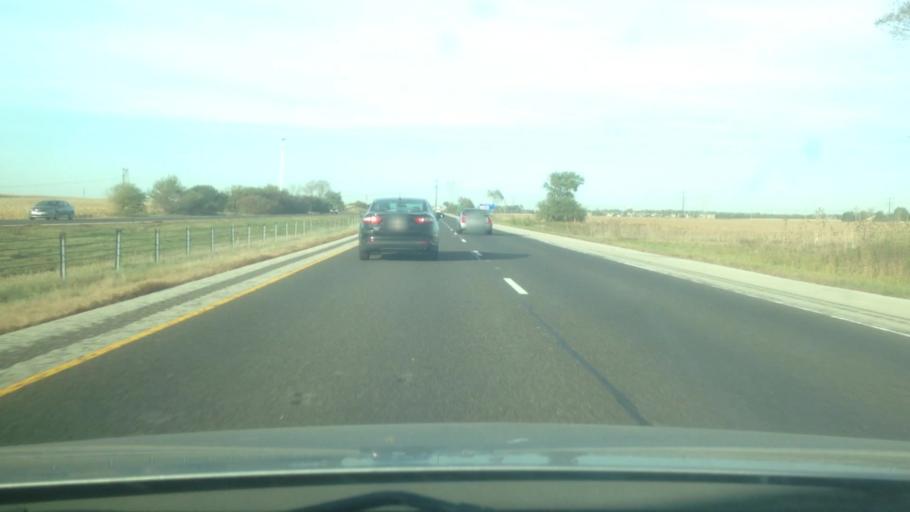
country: US
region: Illinois
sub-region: Will County
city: Peotone
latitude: 41.3036
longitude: -87.8265
